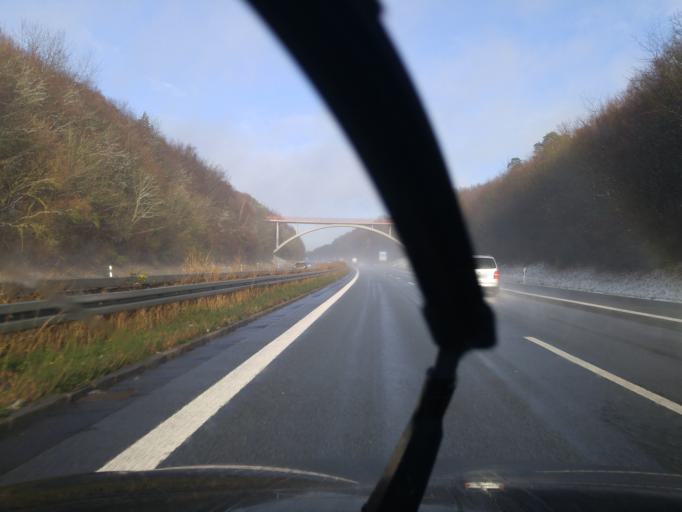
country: DE
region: Bavaria
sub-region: Regierungsbezirk Unterfranken
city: Unterpleichfeld
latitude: 49.8912
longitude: 10.0005
